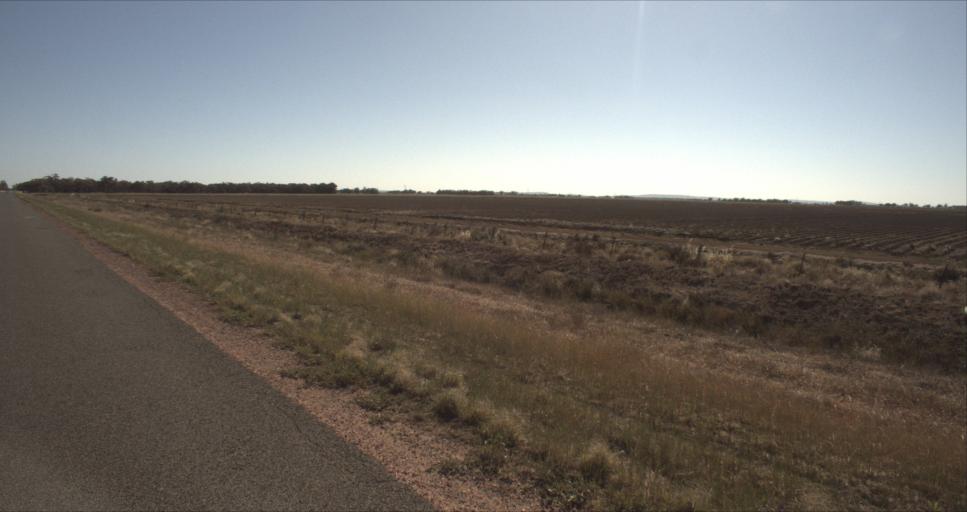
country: AU
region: New South Wales
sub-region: Leeton
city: Leeton
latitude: -34.5700
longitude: 146.2637
